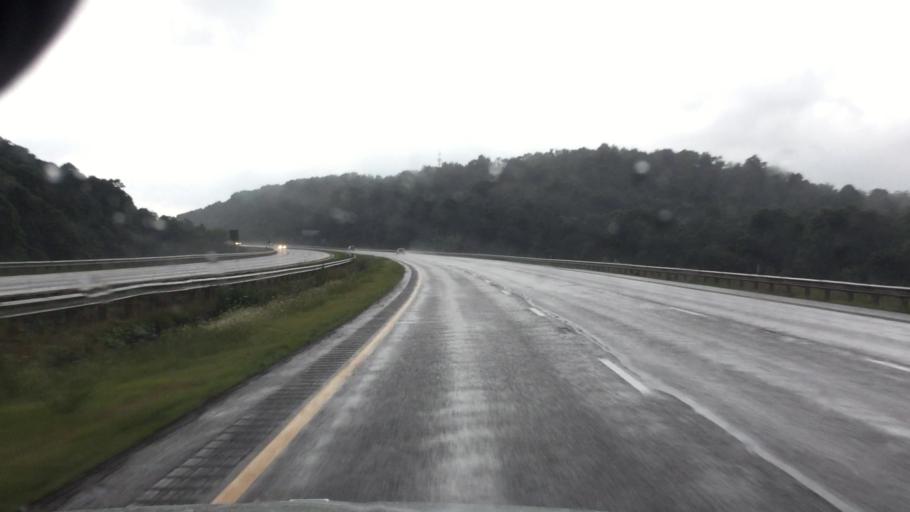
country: US
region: West Virginia
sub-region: Preston County
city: Terra Alta
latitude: 39.6631
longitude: -79.4720
